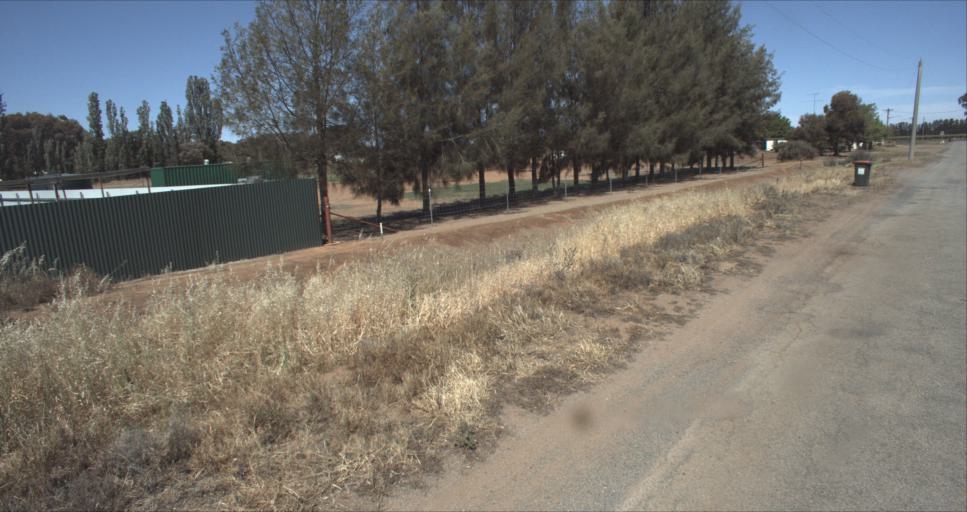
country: AU
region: New South Wales
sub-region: Leeton
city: Leeton
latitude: -34.5284
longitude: 146.3310
